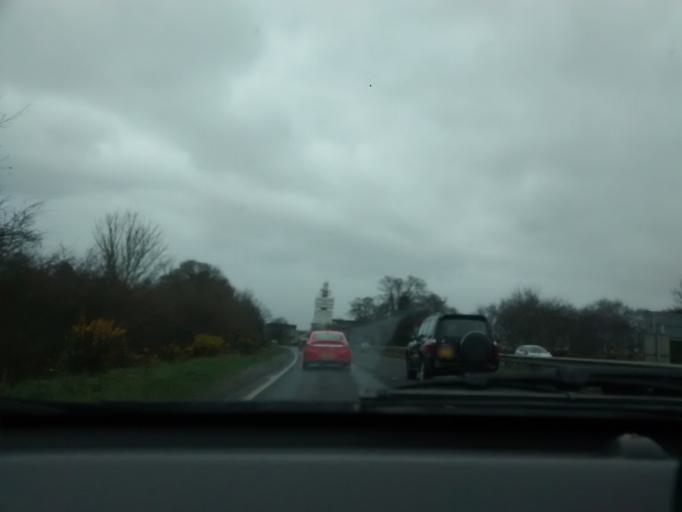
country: GB
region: England
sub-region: Suffolk
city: Kesgrave
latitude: 52.0504
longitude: 1.2772
